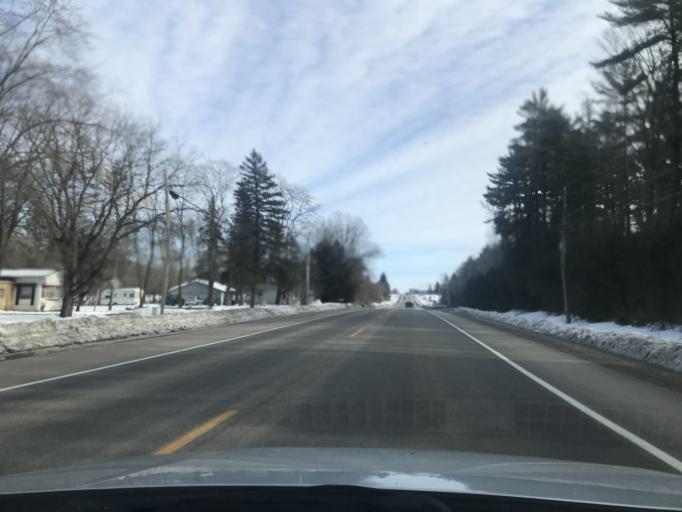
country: US
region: Wisconsin
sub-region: Oconto County
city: Gillett
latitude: 44.8965
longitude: -88.2867
